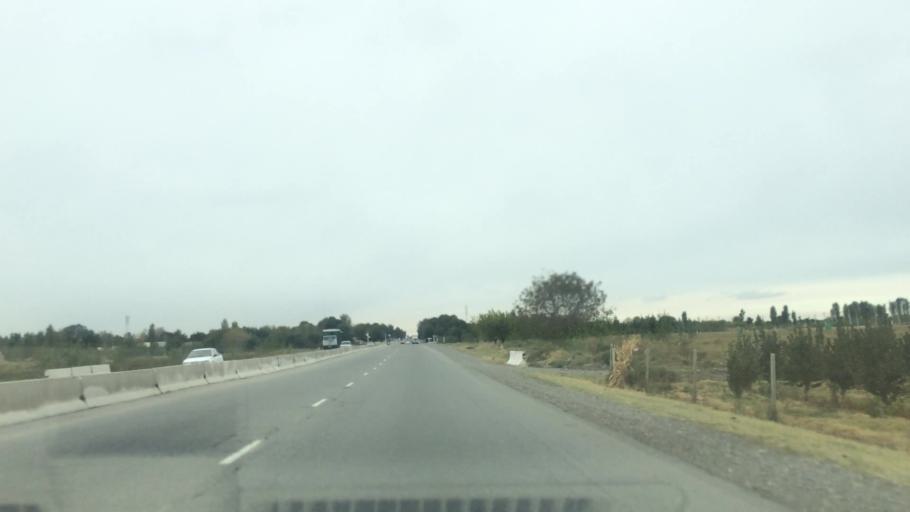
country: UZ
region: Samarqand
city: Bulung'ur
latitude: 39.7397
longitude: 67.1909
